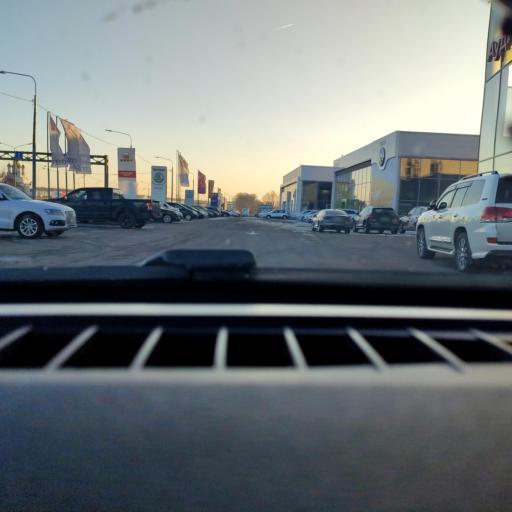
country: RU
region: Voronezj
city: Podgornoye
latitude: 51.7959
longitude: 39.2003
